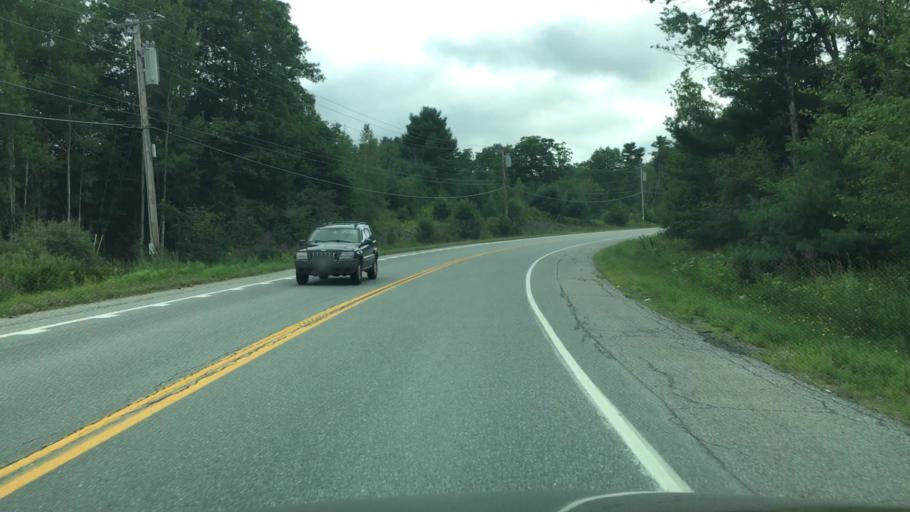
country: US
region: Maine
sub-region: Waldo County
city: Frankfort
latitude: 44.6247
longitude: -68.8689
